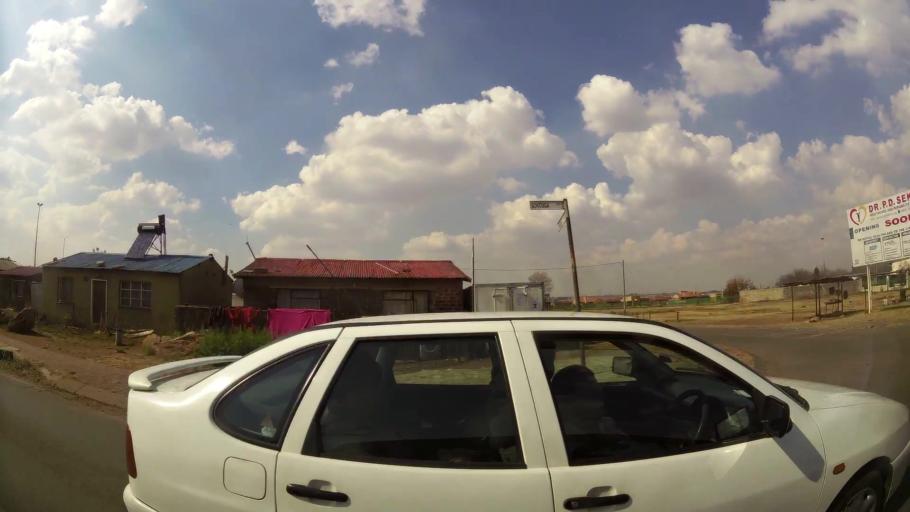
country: ZA
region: Gauteng
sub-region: Ekurhuleni Metropolitan Municipality
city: Germiston
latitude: -26.3332
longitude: 28.1618
